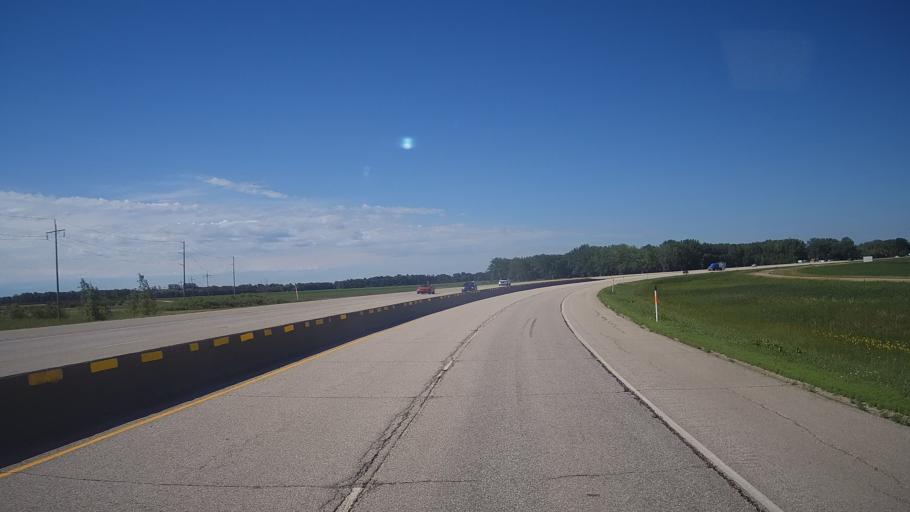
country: CA
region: Manitoba
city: Portage la Prairie
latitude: 49.9638
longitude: -98.2374
